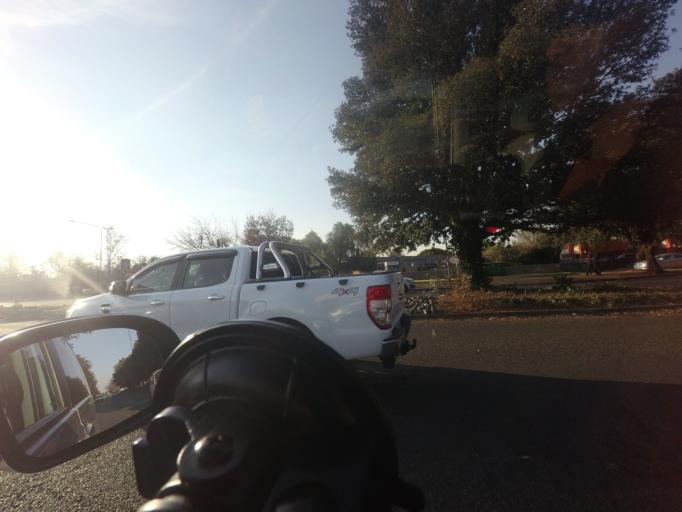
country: ZA
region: Gauteng
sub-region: Sedibeng District Municipality
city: Vereeniging
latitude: -26.6583
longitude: 27.9663
